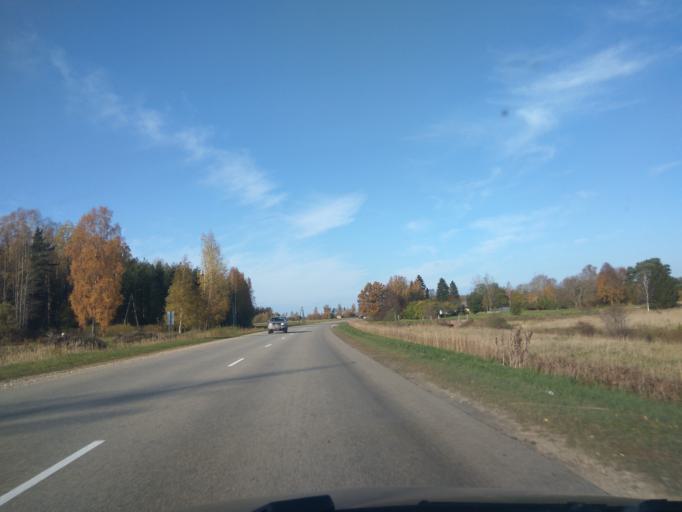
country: LV
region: Ventspils
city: Ventspils
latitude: 57.2871
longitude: 21.5674
